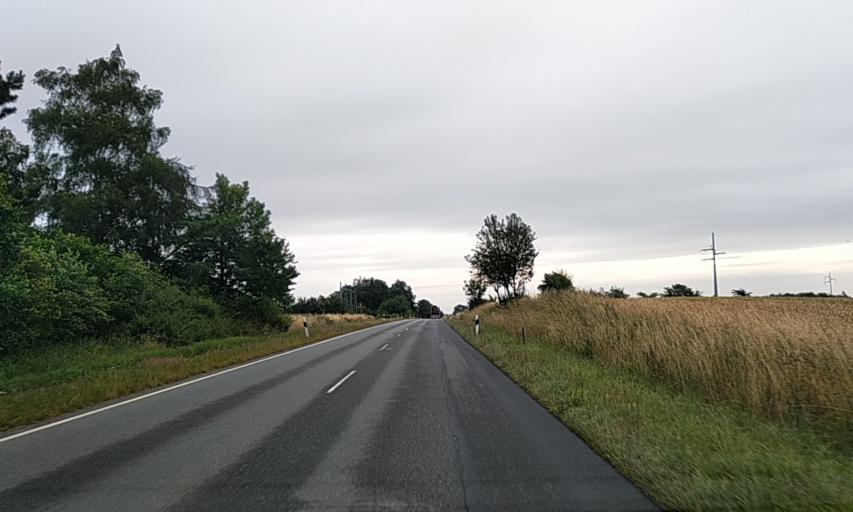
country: DE
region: Schleswig-Holstein
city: Struxdorf
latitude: 54.6288
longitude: 9.6411
